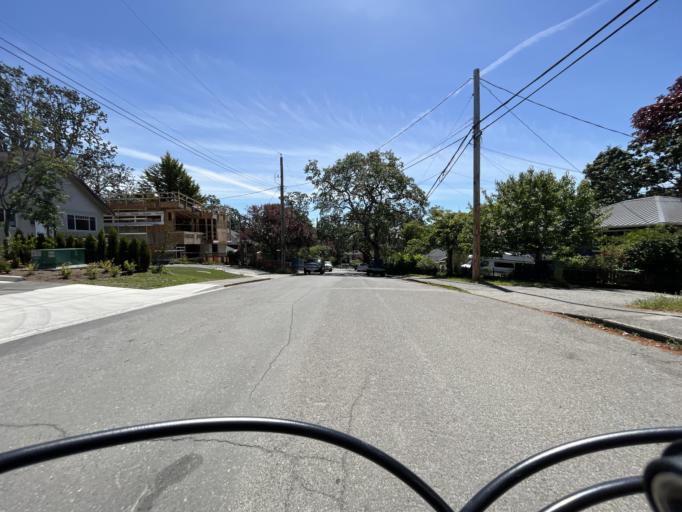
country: CA
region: British Columbia
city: Victoria
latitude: 48.4452
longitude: -123.3578
